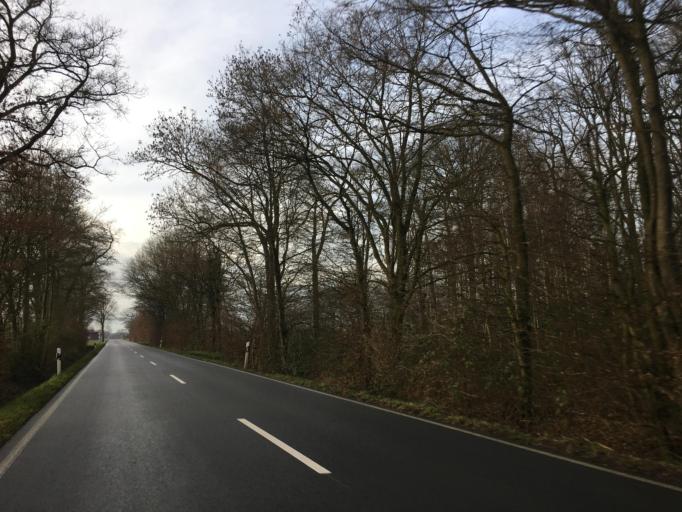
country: DE
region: North Rhine-Westphalia
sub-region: Regierungsbezirk Munster
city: Dulmen
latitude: 51.8239
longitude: 7.3488
